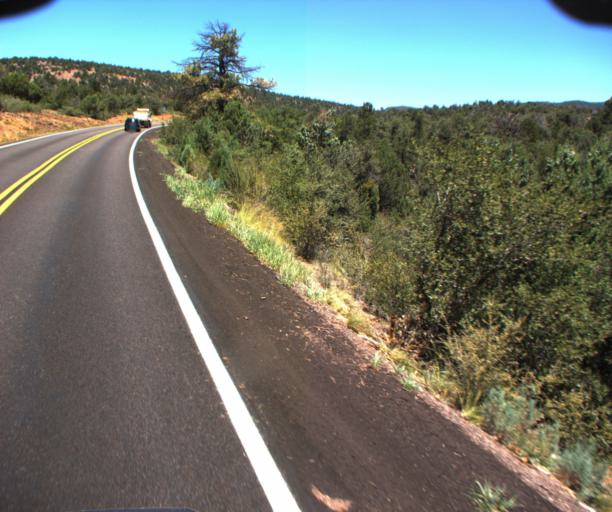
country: US
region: Arizona
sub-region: Gila County
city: Pine
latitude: 34.3423
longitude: -111.4253
